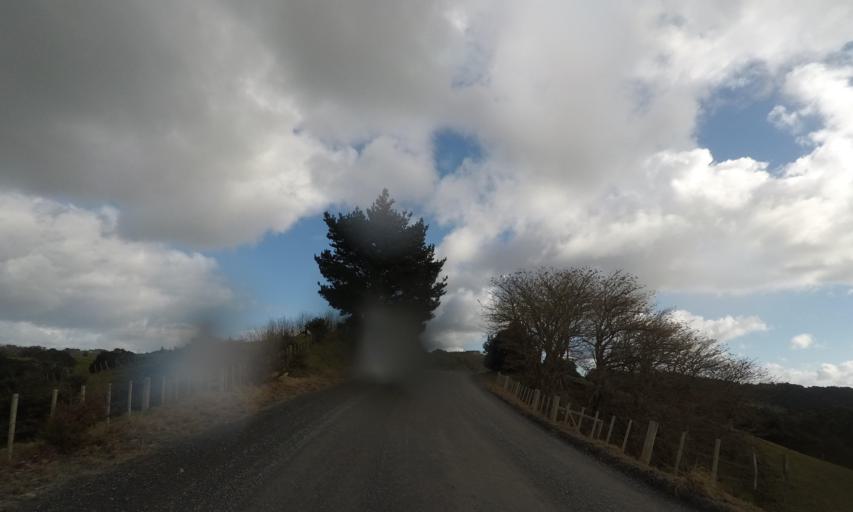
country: NZ
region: Auckland
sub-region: Auckland
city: Wellsford
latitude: -36.1726
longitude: 174.5897
